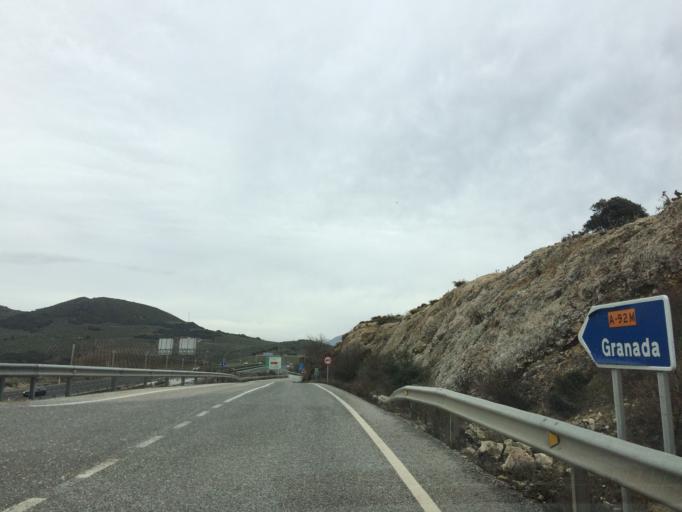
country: ES
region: Andalusia
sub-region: Provincia de Malaga
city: Casabermeja
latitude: 36.9685
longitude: -4.4391
